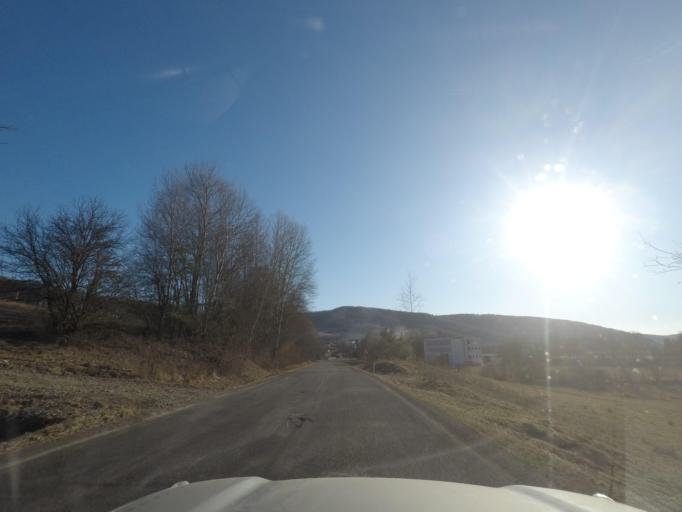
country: SK
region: Presovsky
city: Medzilaborce
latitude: 49.2594
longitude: 21.7929
